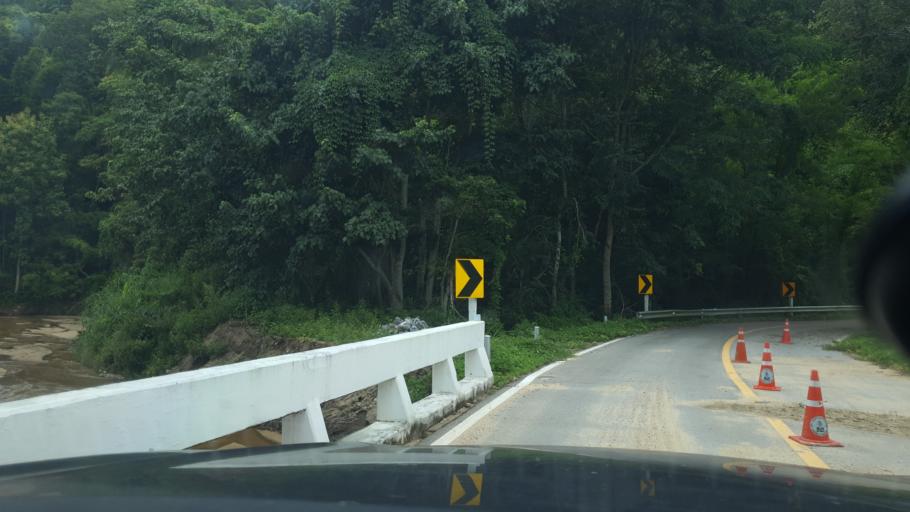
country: TH
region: Lamphun
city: Mae Tha
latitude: 18.4418
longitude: 99.2682
